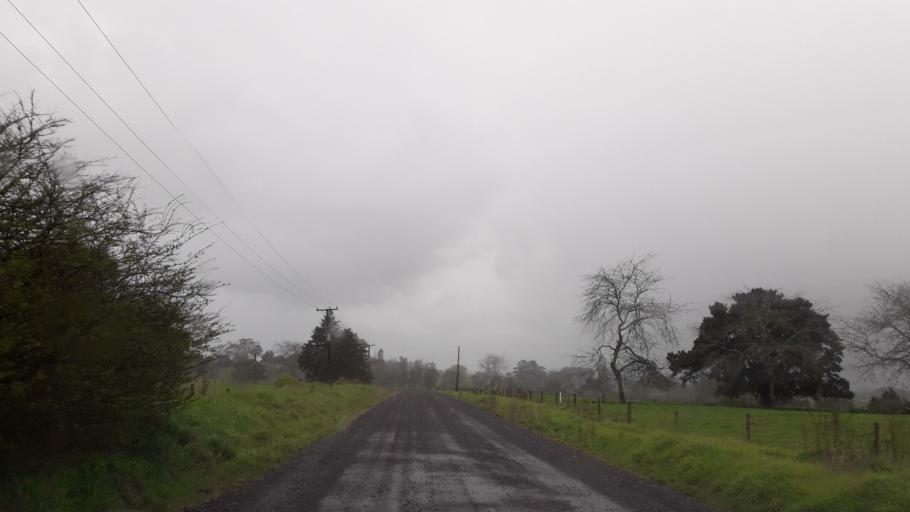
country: NZ
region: Northland
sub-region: Far North District
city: Waimate North
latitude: -35.4762
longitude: 173.6923
